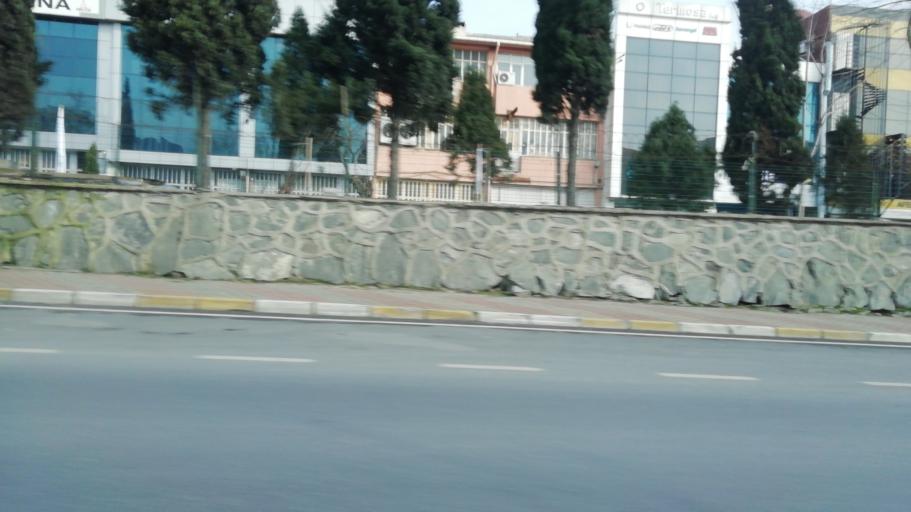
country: TR
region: Istanbul
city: Basaksehir
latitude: 41.0942
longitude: 28.7936
